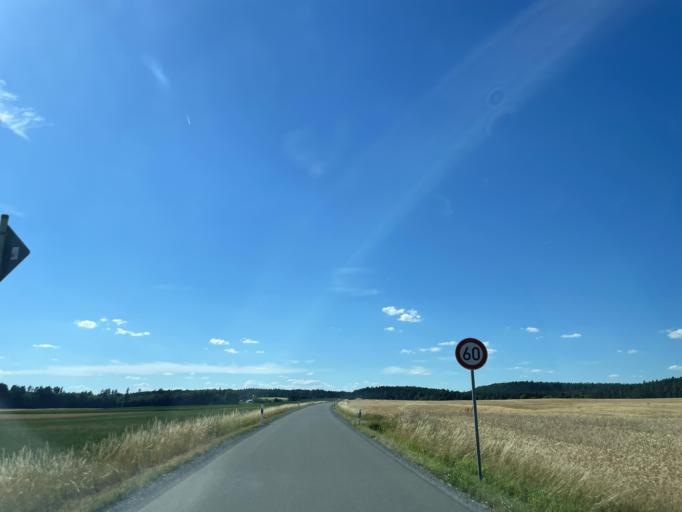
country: DE
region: Bavaria
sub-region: Upper Palatinate
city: Speinshart
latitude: 49.7843
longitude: 11.8421
